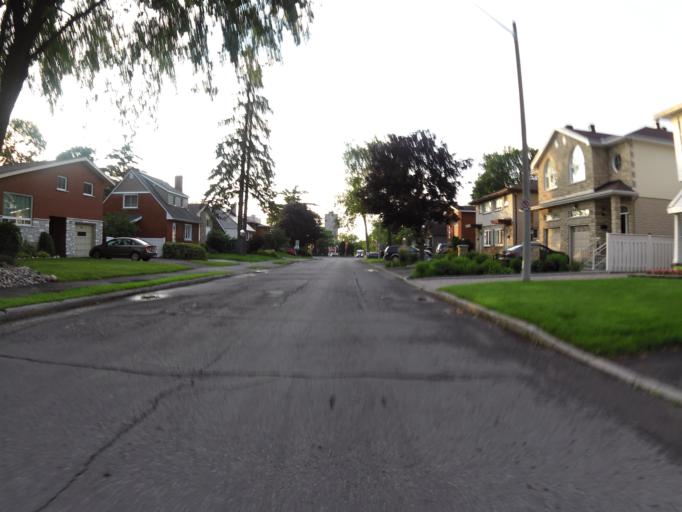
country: CA
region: Ontario
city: Bells Corners
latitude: 45.3609
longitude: -75.7883
